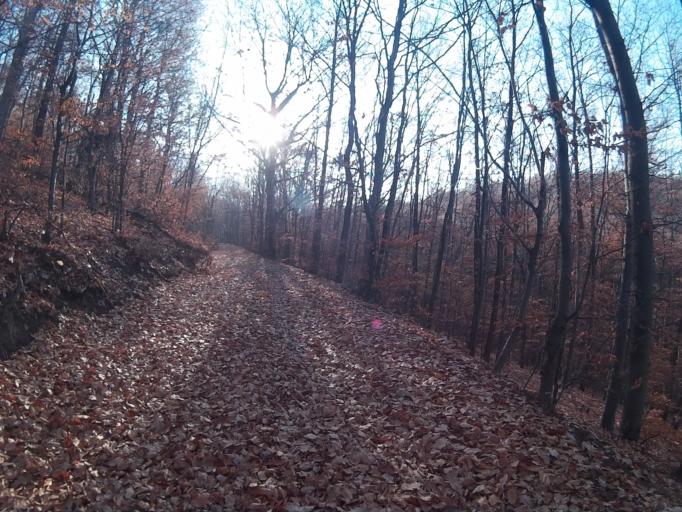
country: HU
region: Heves
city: Belapatfalva
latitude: 48.0276
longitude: 20.3699
